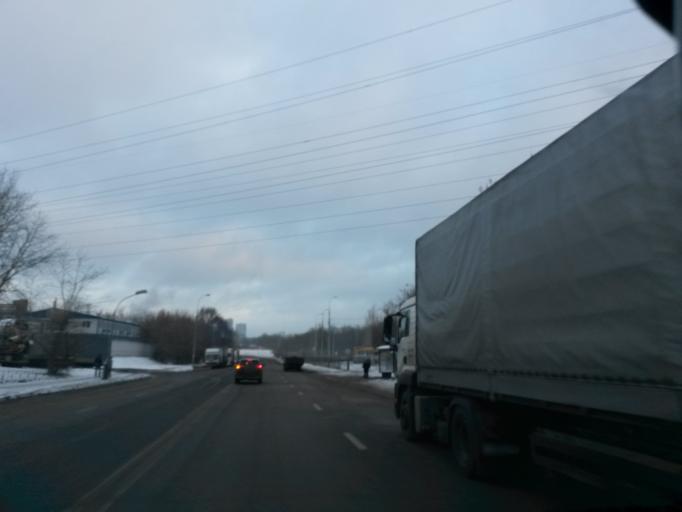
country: RU
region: Moscow
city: Amin'yevo
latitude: 55.7011
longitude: 37.4520
